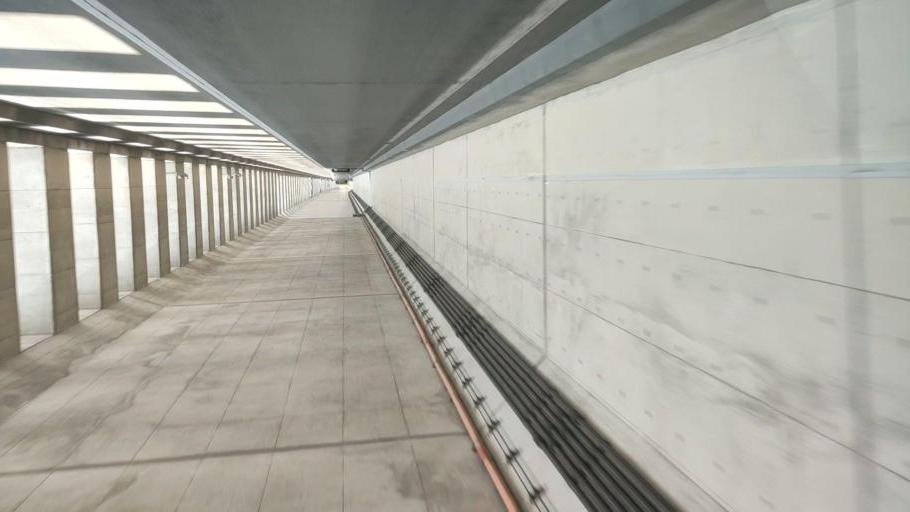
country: JP
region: Hokkaido
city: Rumoi
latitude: 43.6703
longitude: 141.3485
